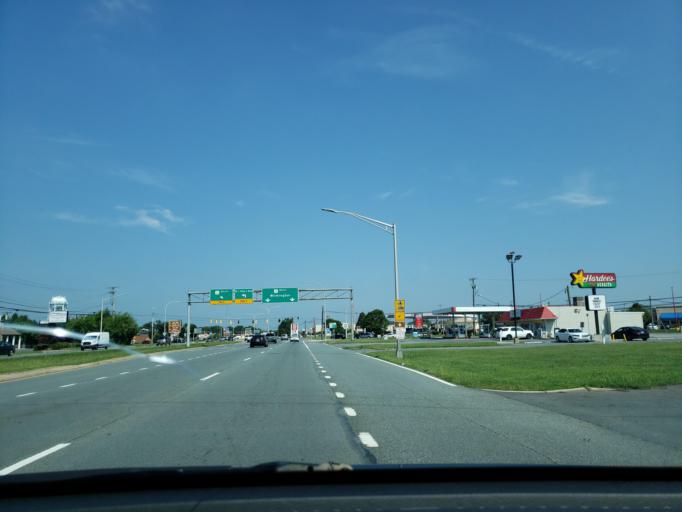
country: US
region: Delaware
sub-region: Kent County
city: Dover
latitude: 39.1562
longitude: -75.5088
